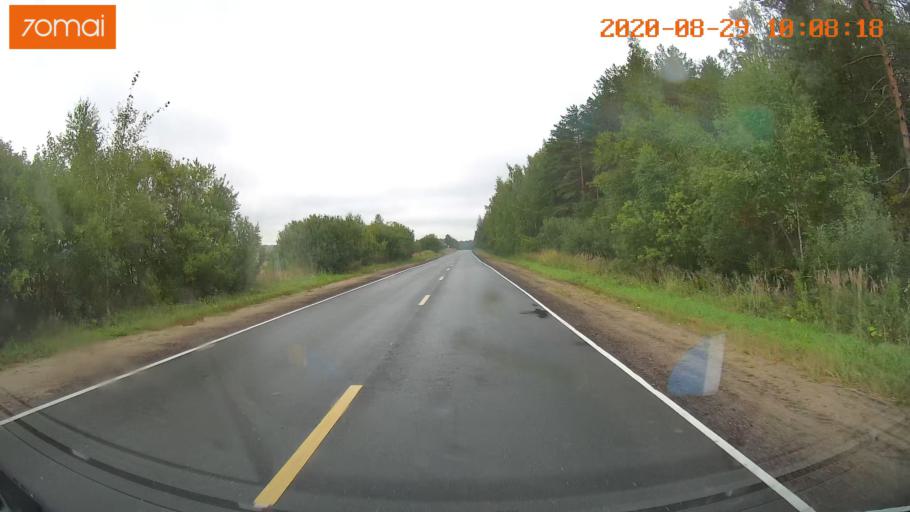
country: RU
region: Ivanovo
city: Kuznechikha
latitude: 57.3765
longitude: 42.5864
